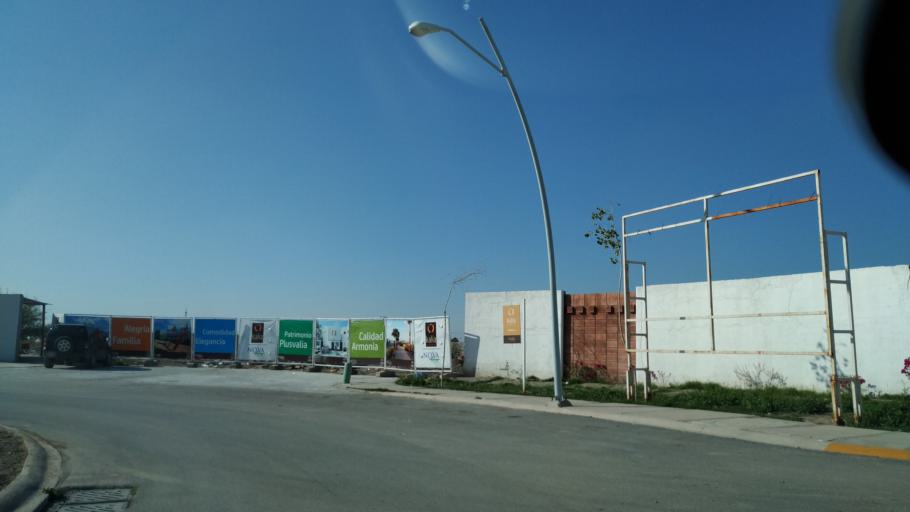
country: MX
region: Coahuila
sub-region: Torreon
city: Fraccionamiento la Noria
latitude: 25.5422
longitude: -103.3485
